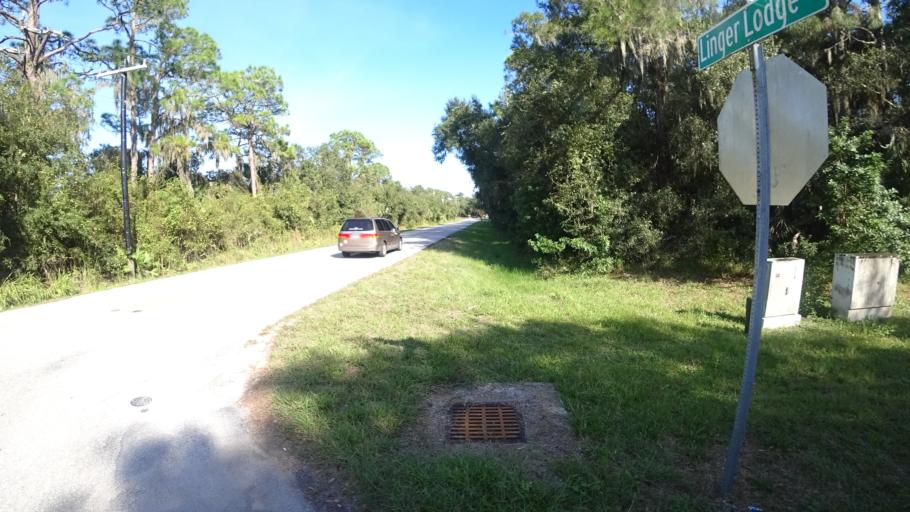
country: US
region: Florida
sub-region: Sarasota County
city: The Meadows
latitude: 27.4177
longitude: -82.4504
